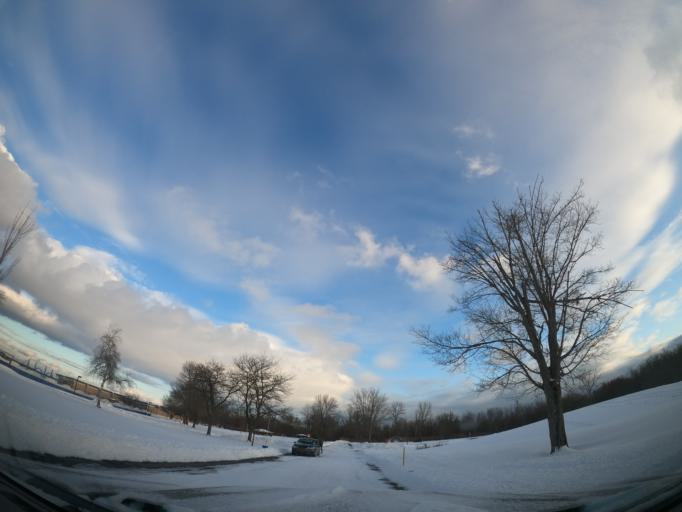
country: US
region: New York
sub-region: Onondaga County
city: Brewerton
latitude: 43.2244
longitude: -76.1093
